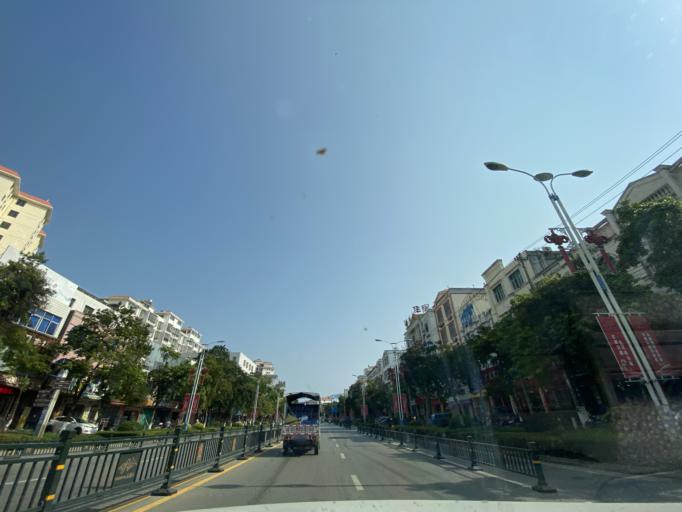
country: CN
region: Hainan
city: Chongshan
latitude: 18.7707
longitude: 109.5167
